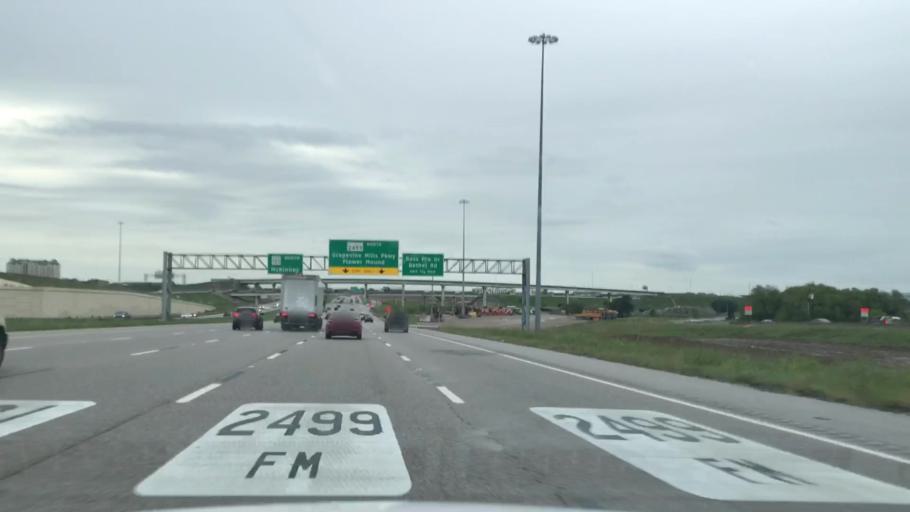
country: US
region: Texas
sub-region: Dallas County
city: Coppell
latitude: 32.9445
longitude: -97.0399
